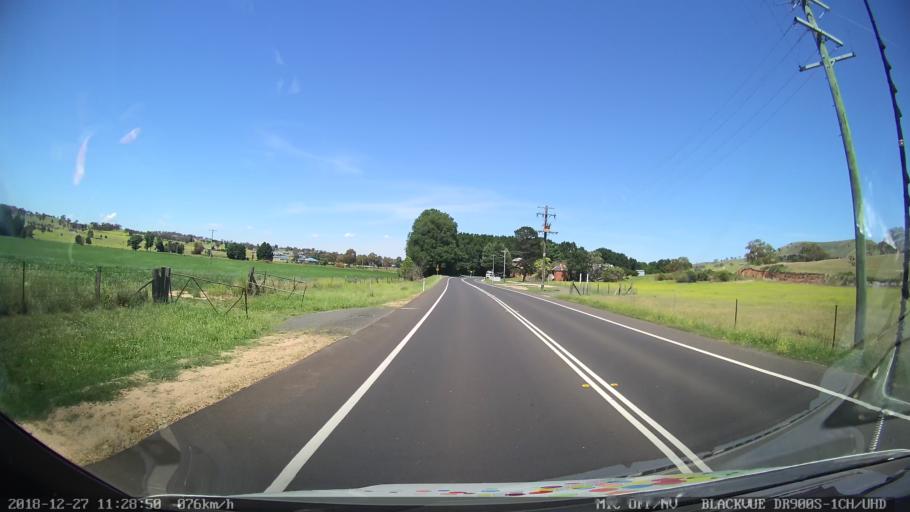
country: AU
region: New South Wales
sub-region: Bathurst Regional
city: Perthville
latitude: -33.4810
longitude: 149.5595
